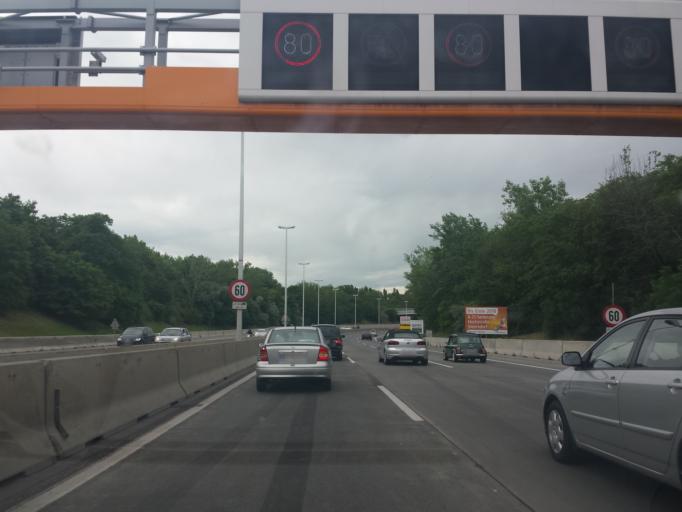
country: AT
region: Lower Austria
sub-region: Politischer Bezirk Wien-Umgebung
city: Leopoldsdorf
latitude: 48.1544
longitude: 16.3748
